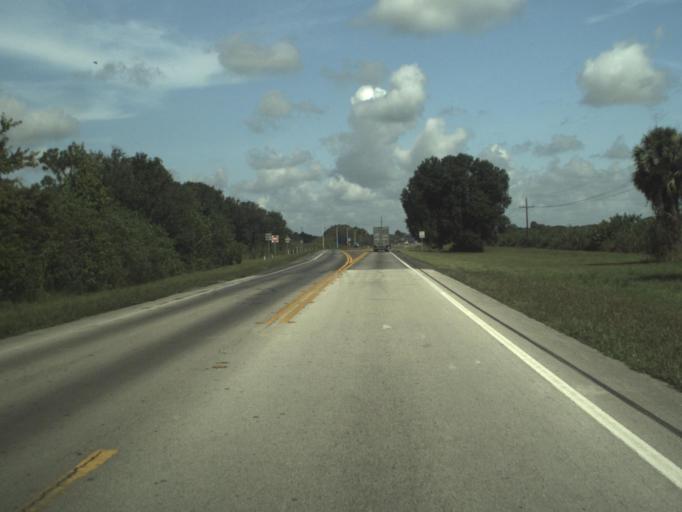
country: US
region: Florida
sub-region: Martin County
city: Indiantown
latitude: 27.0040
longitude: -80.4430
